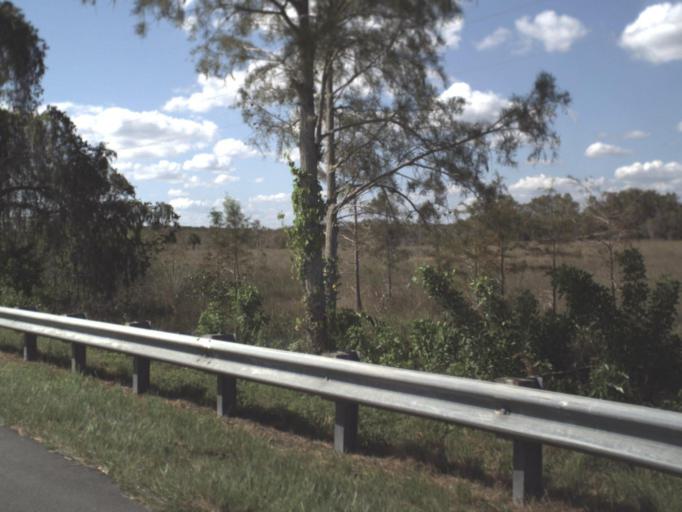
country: US
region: Florida
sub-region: Collier County
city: Immokalee
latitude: 25.8622
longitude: -81.0857
